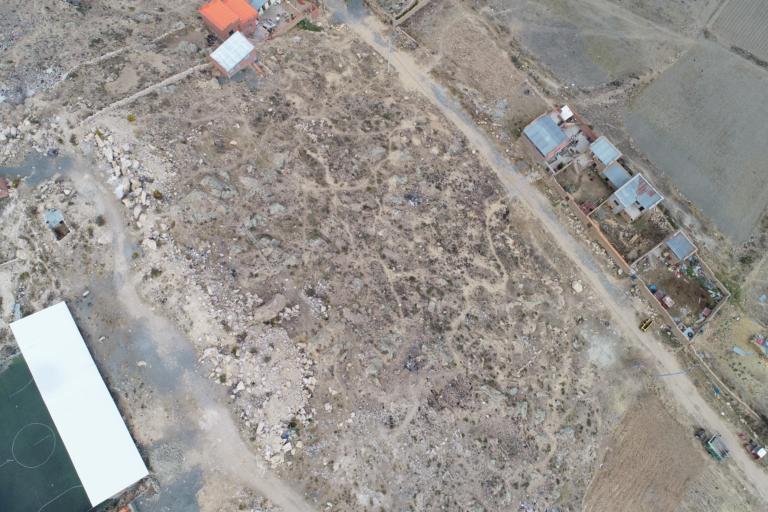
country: BO
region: La Paz
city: Achacachi
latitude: -16.0422
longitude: -68.6810
